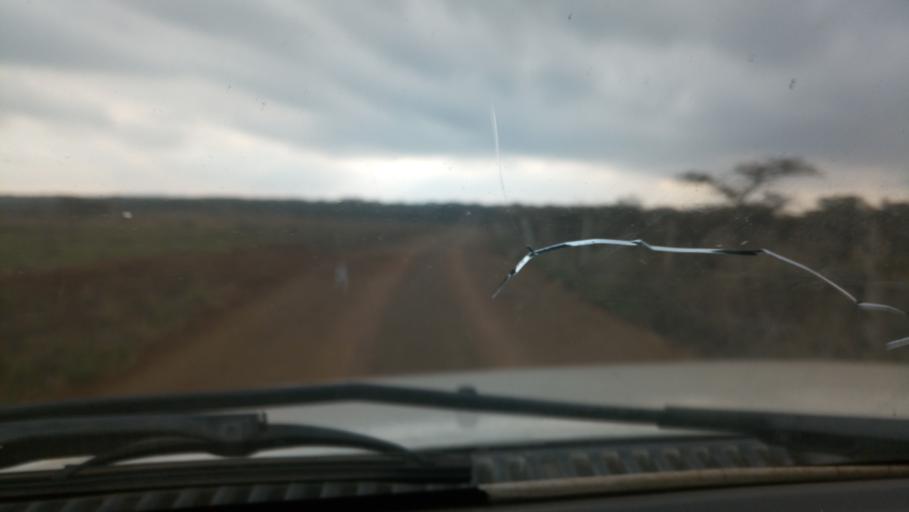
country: KE
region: Nairobi Area
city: Nairobi
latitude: -1.3337
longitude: 36.8106
